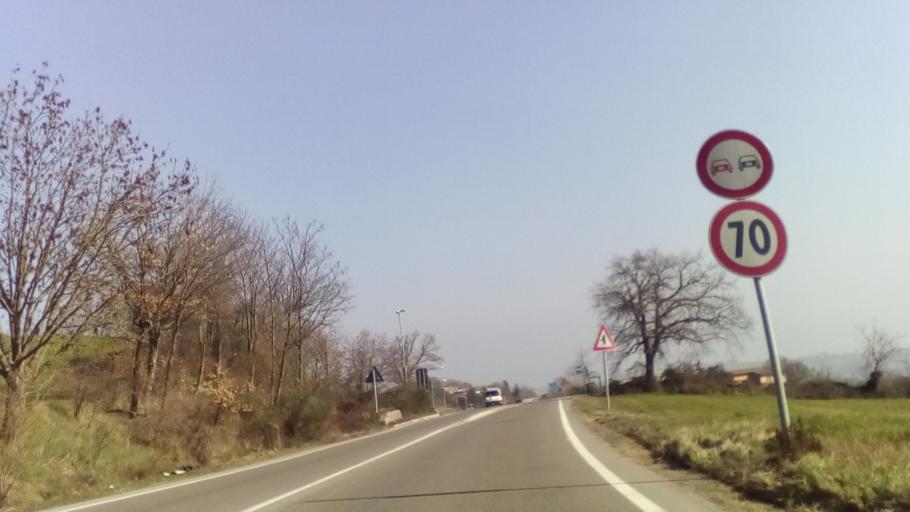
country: IT
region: Emilia-Romagna
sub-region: Provincia di Modena
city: Sant'Antonio
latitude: 44.4082
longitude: 10.8357
